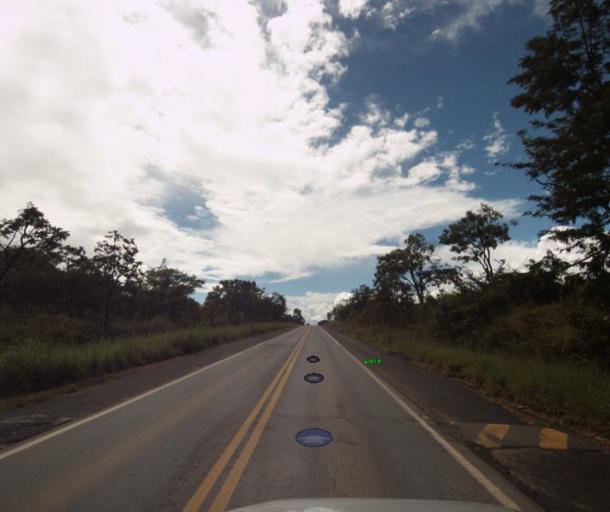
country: BR
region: Goias
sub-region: Uruacu
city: Uruacu
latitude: -14.1887
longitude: -49.1273
